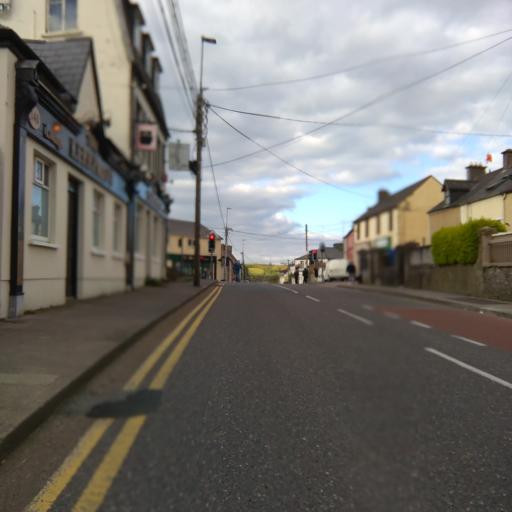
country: IE
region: Munster
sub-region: County Cork
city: Cork
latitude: 51.9086
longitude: -8.4555
